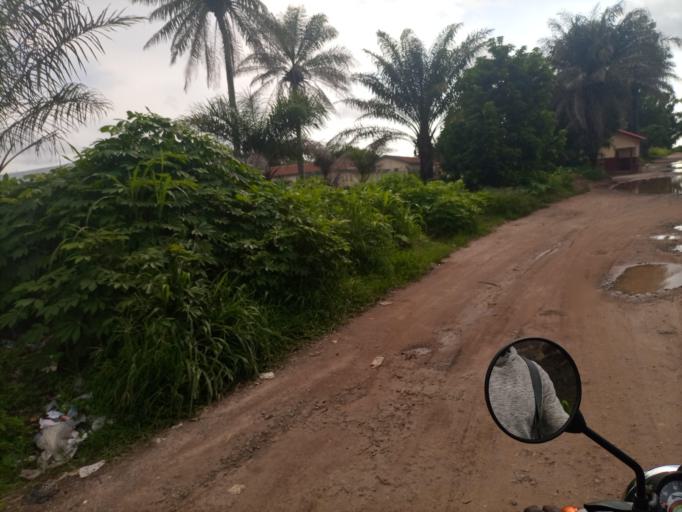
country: SL
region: Northern Province
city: Masoyila
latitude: 8.6091
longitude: -13.1803
